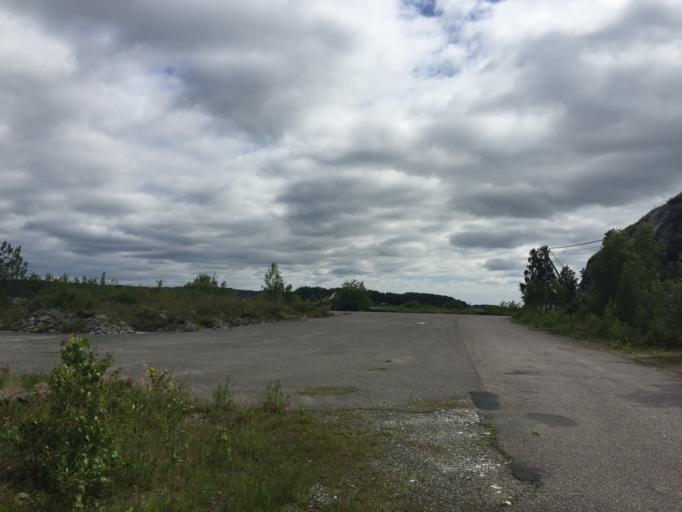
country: SE
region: Stockholm
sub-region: Nynashamns Kommun
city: Osmo
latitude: 58.9731
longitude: 17.7190
